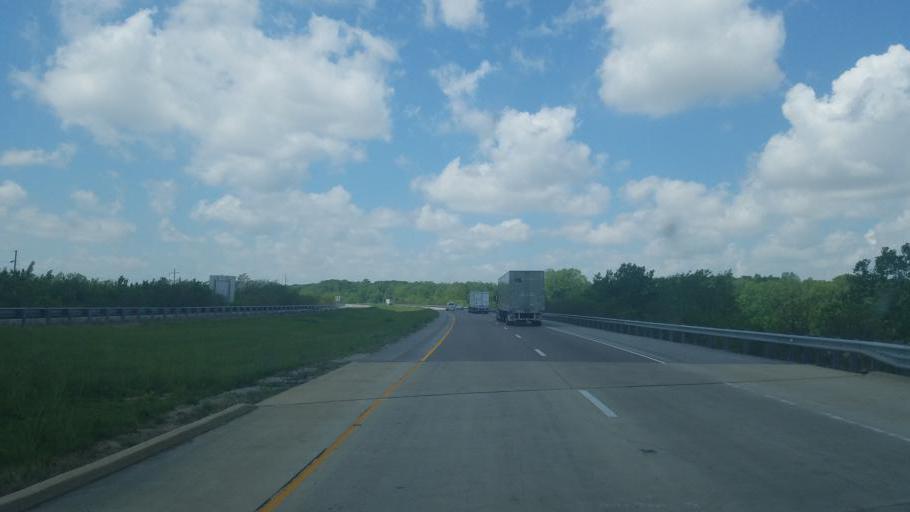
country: US
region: Illinois
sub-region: Cumberland County
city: Greenup
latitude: 39.2533
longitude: -88.1754
